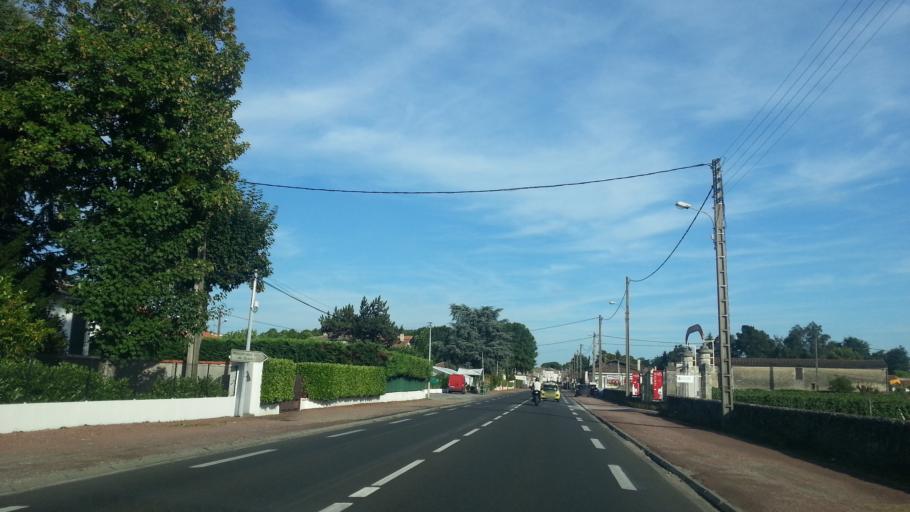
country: FR
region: Aquitaine
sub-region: Departement de la Gironde
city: Podensac
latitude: 44.6544
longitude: -0.3619
